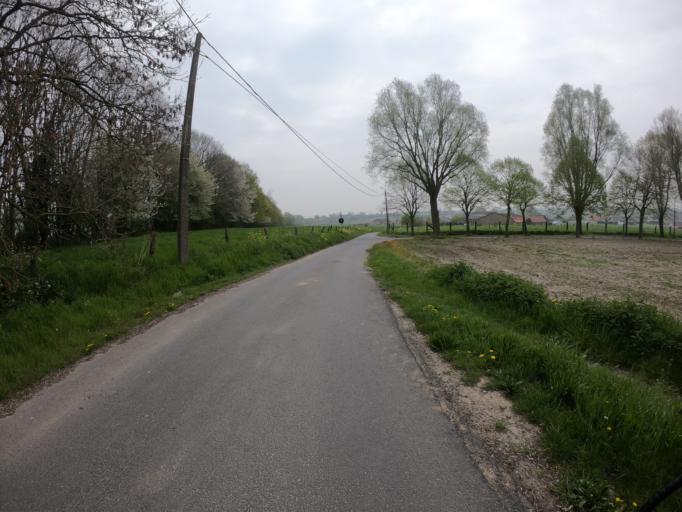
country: BE
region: Flanders
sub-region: Provincie West-Vlaanderen
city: Zwevegem
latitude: 50.7816
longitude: 3.3830
